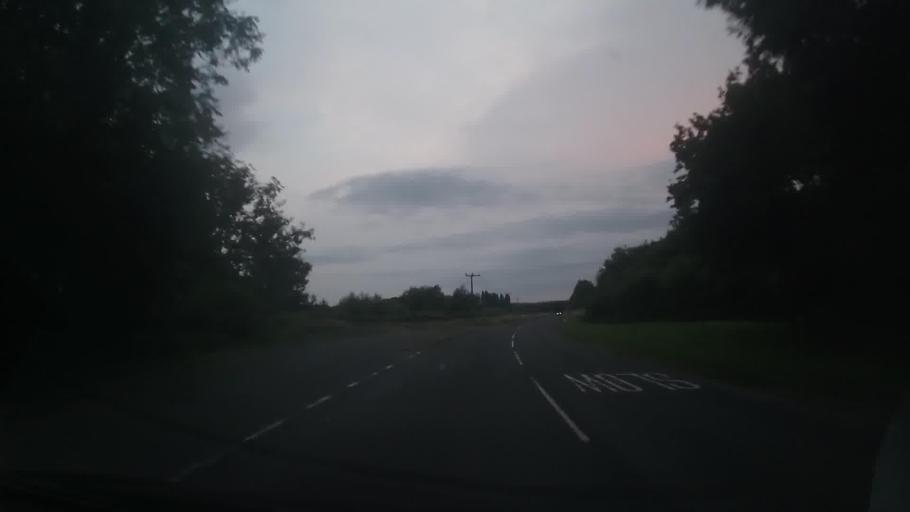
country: GB
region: England
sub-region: Leicestershire
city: Sileby
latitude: 52.7115
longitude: -1.1126
